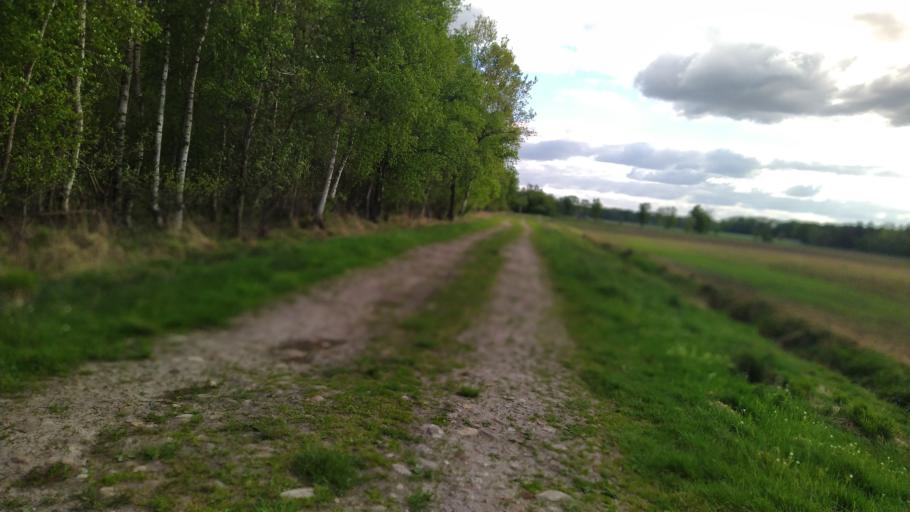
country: DE
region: Lower Saxony
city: Brest
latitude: 53.4112
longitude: 9.3839
